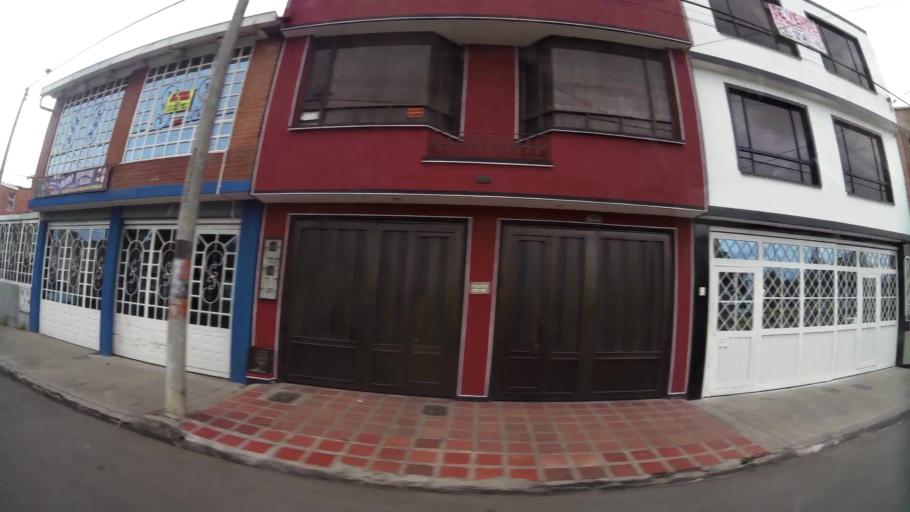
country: CO
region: Bogota D.C.
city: Bogota
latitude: 4.6084
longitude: -74.1150
